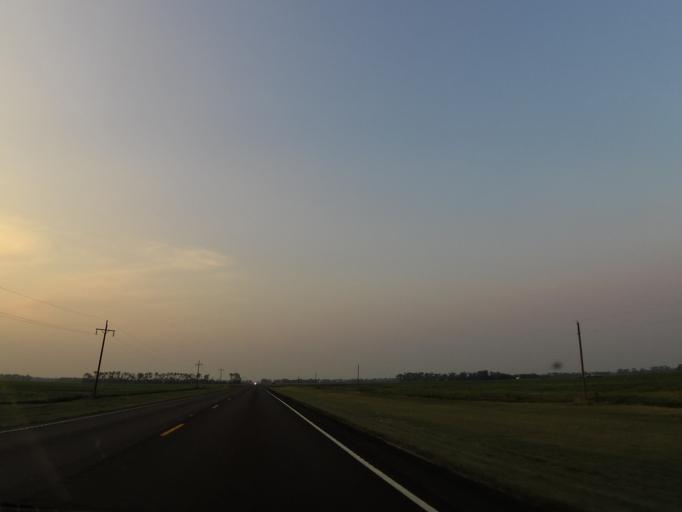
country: US
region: North Dakota
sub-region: Walsh County
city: Park River
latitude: 48.3148
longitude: -97.6224
